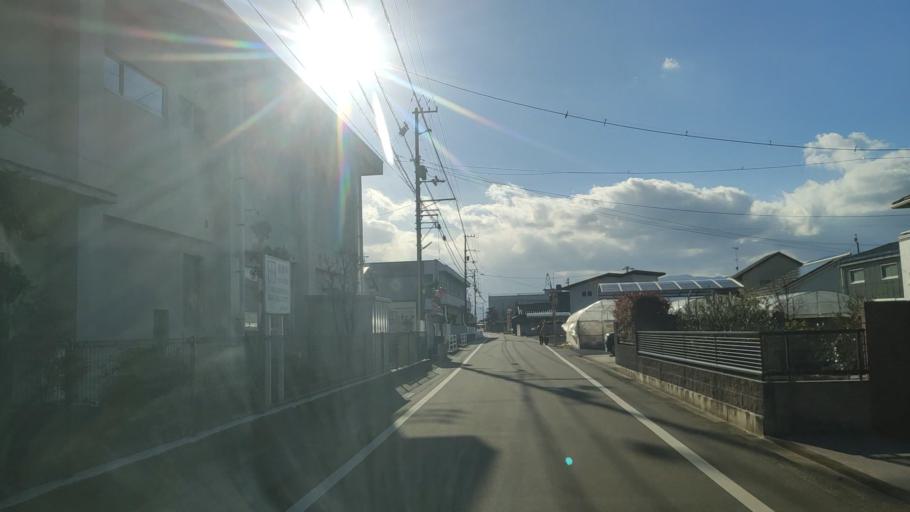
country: JP
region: Ehime
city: Saijo
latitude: 33.9140
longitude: 133.1013
